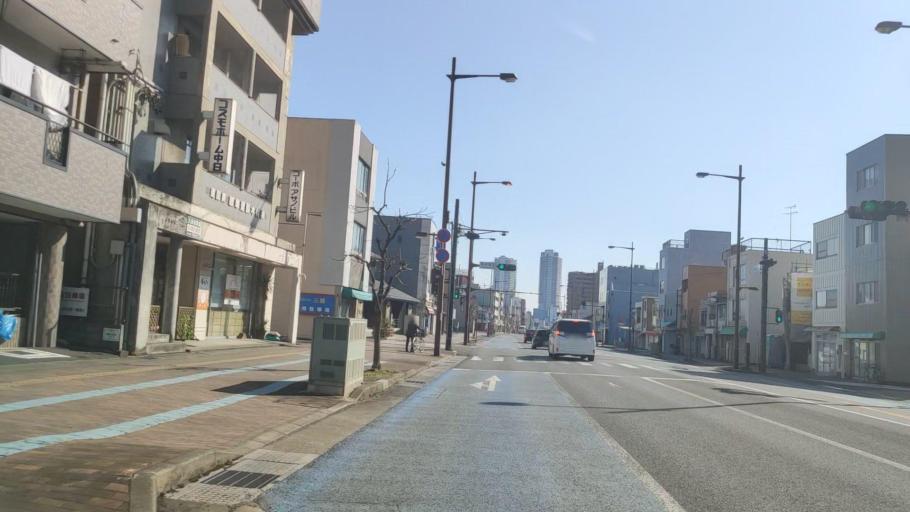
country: JP
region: Gifu
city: Gifu-shi
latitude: 35.4228
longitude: 136.7520
